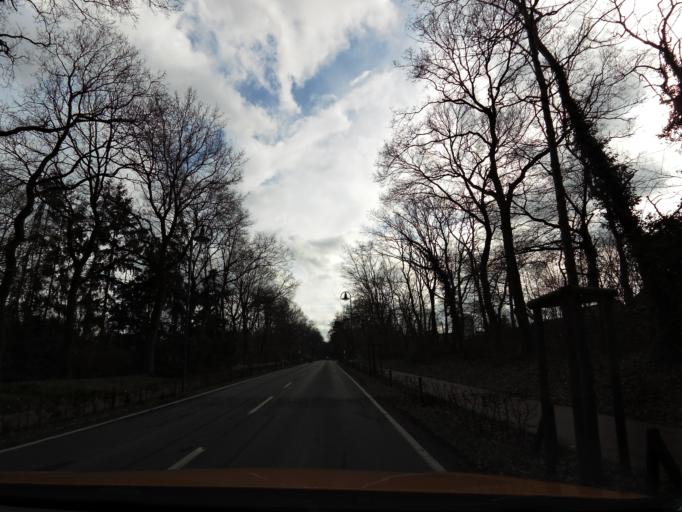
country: DE
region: Lower Saxony
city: Dotlingen
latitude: 52.9713
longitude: 8.3983
